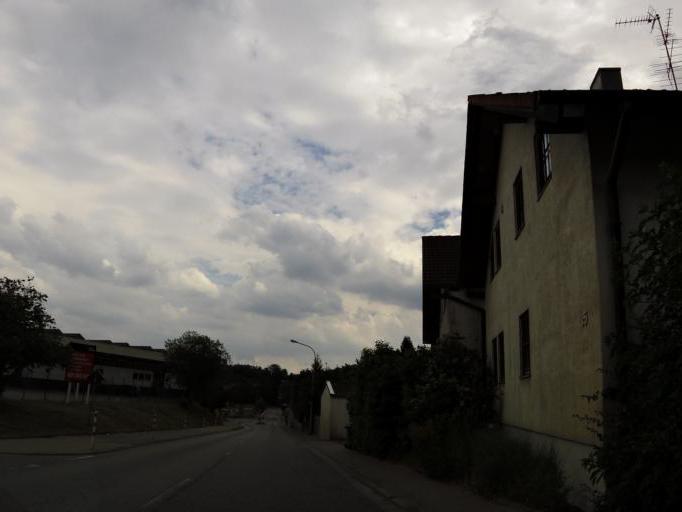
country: DE
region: Hesse
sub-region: Regierungsbezirk Darmstadt
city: Messel
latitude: 49.9229
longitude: 8.7438
